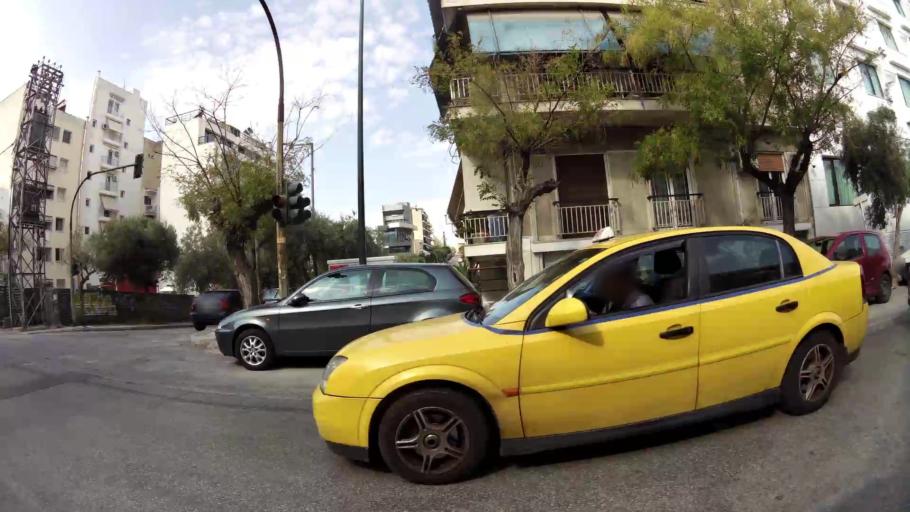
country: GR
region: Attica
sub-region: Nomarchia Athinas
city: Nea Smyrni
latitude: 37.9568
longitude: 23.7185
